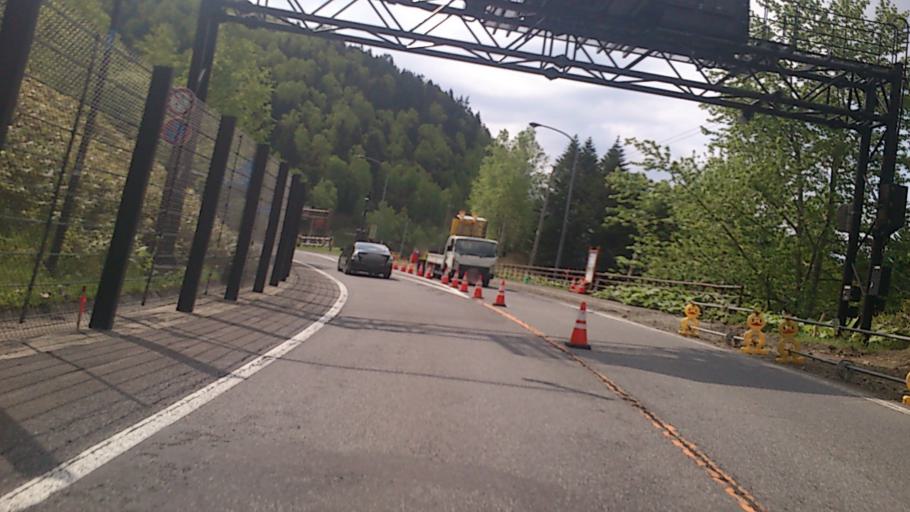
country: JP
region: Hokkaido
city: Kamikawa
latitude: 43.6819
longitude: 143.0356
